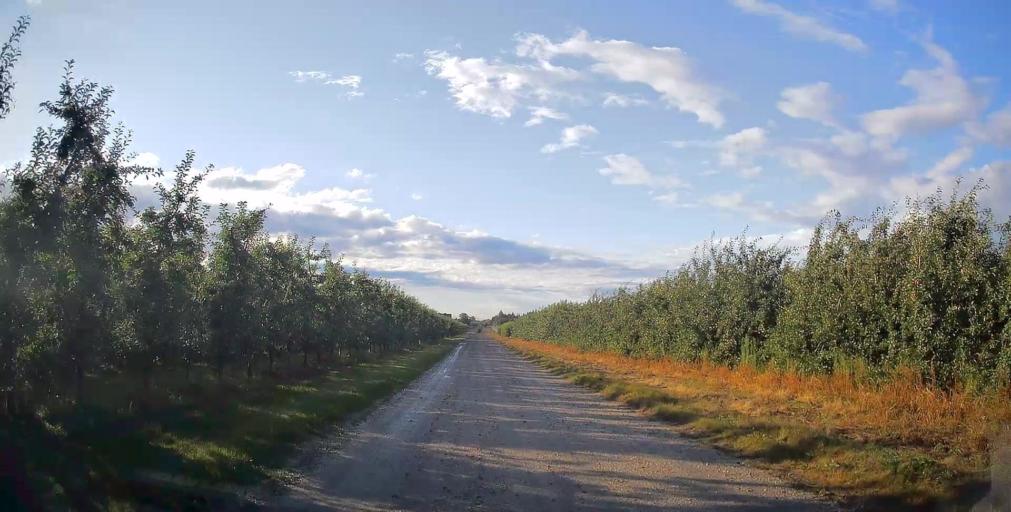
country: PL
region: Masovian Voivodeship
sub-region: Powiat grojecki
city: Goszczyn
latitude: 51.7466
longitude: 20.8870
